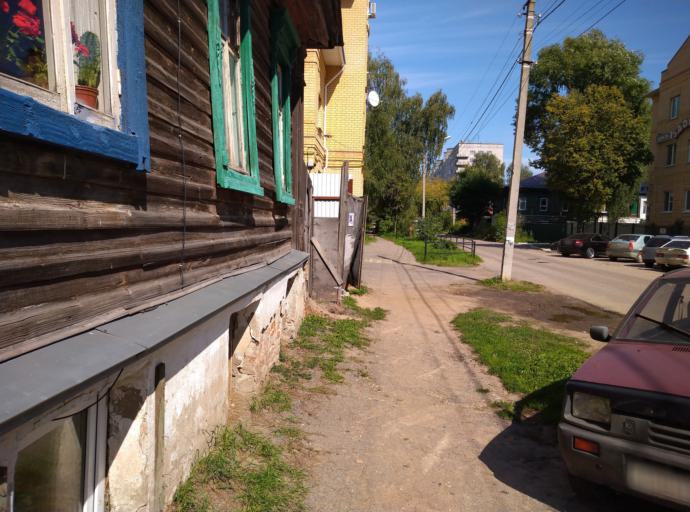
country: RU
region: Kostroma
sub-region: Kostromskoy Rayon
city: Kostroma
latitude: 57.7701
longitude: 40.9360
